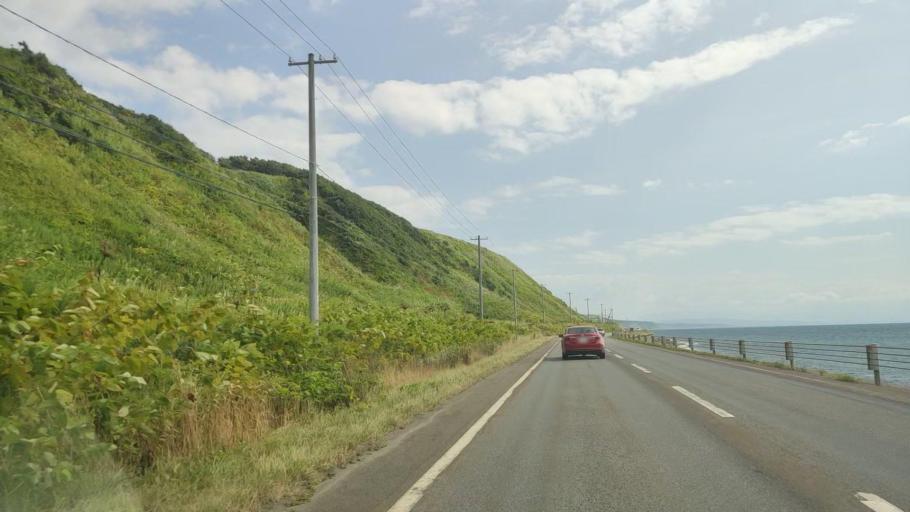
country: JP
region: Hokkaido
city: Rumoi
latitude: 44.0942
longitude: 141.6608
